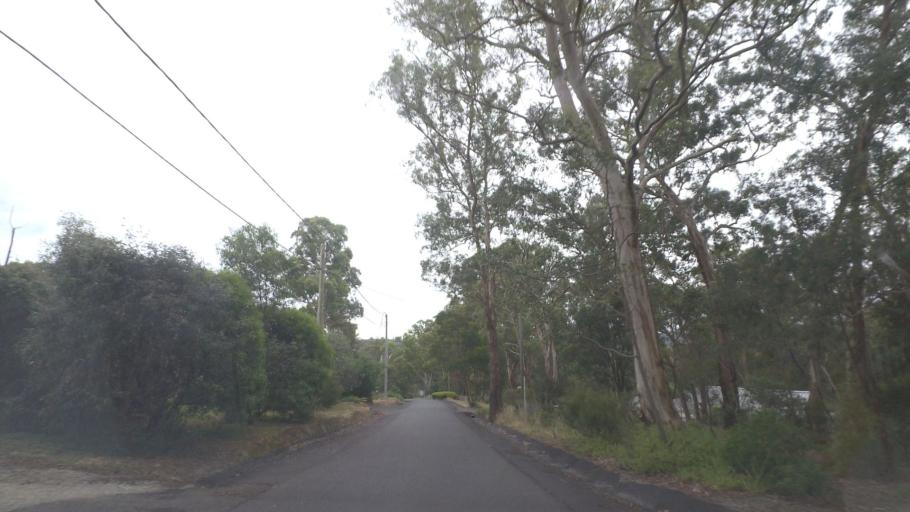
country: AU
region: Victoria
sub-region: Manningham
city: Warrandyte
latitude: -37.7524
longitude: 145.2110
